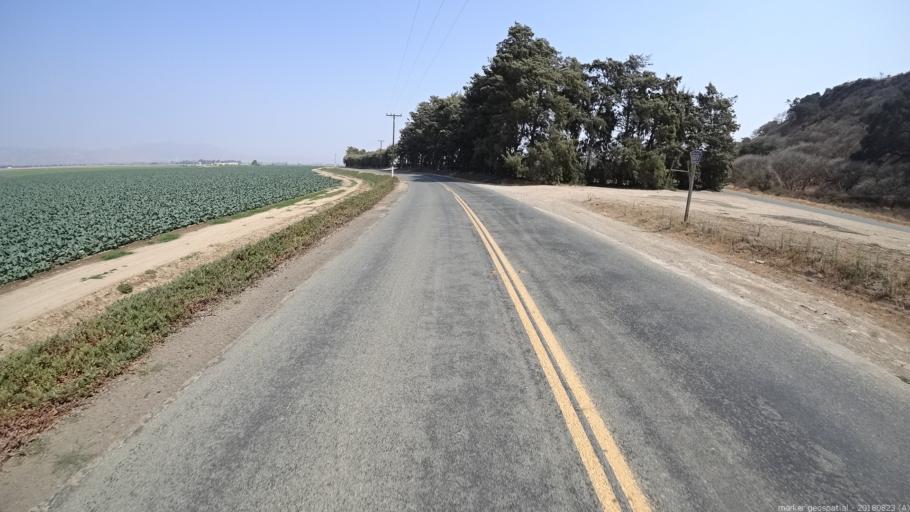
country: US
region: California
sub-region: Monterey County
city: Soledad
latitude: 36.4122
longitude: -121.3915
